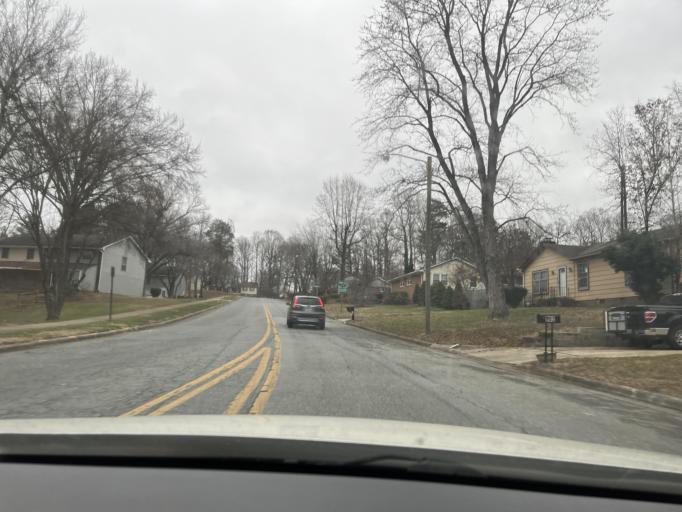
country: US
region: North Carolina
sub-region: Guilford County
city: Greensboro
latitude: 36.0208
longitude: -79.7899
